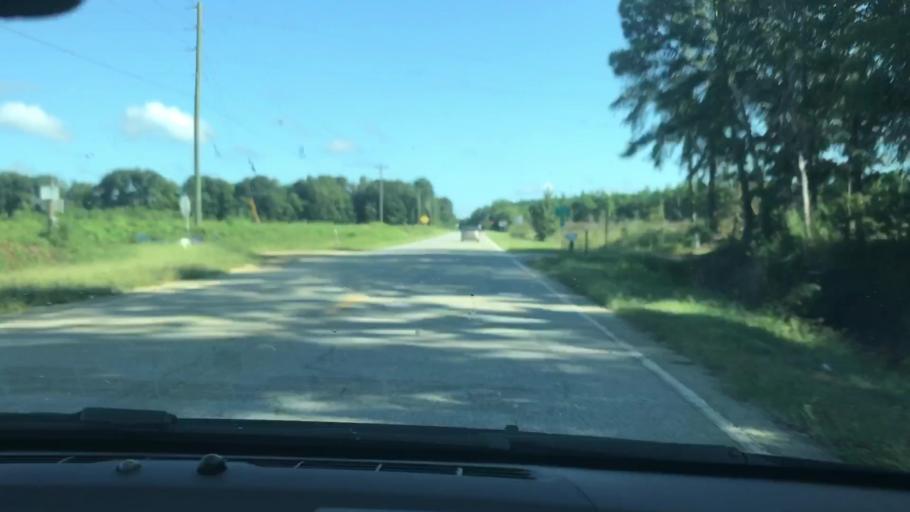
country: US
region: Georgia
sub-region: Quitman County
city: Georgetown
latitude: 31.7790
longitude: -85.0917
